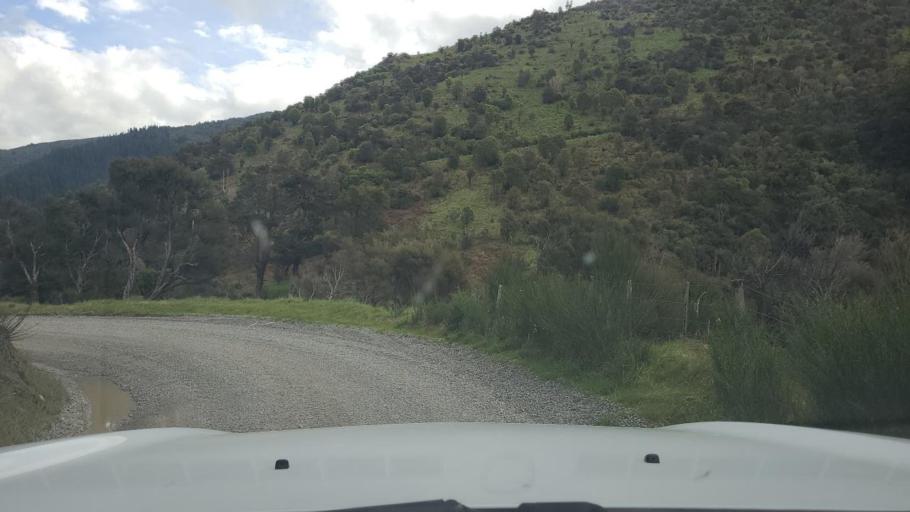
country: NZ
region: Wellington
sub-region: Masterton District
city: Masterton
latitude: -40.9329
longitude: 175.4815
